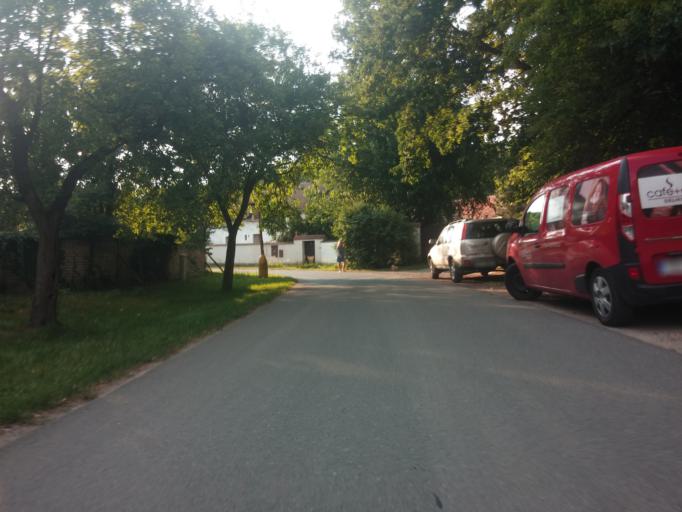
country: CZ
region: Central Bohemia
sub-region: Okres Nymburk
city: Podebrady
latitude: 50.1319
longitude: 15.1125
